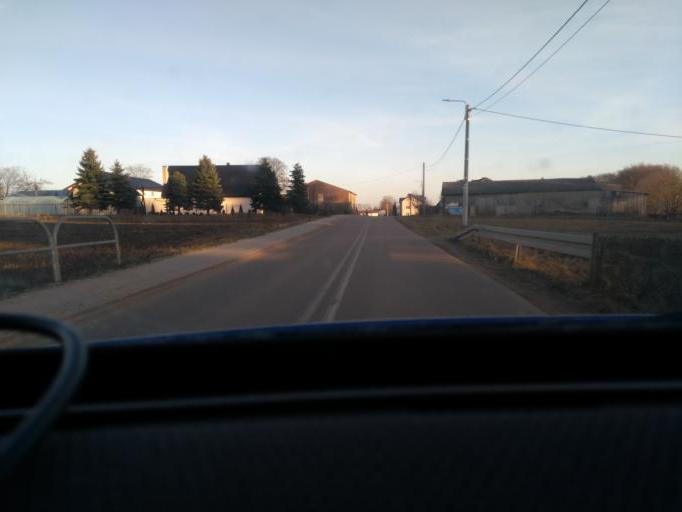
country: PL
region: Pomeranian Voivodeship
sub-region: Powiat kartuski
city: Przodkowo
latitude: 54.4124
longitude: 18.3215
